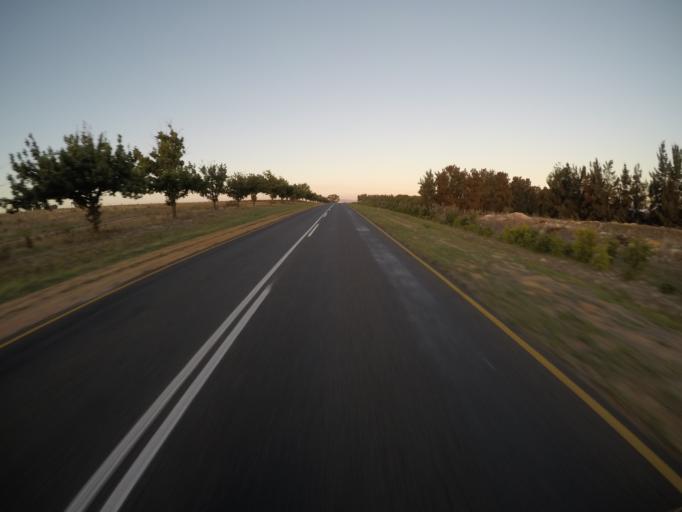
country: ZA
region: Western Cape
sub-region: Cape Winelands District Municipality
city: Paarl
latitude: -33.8051
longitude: 18.8829
